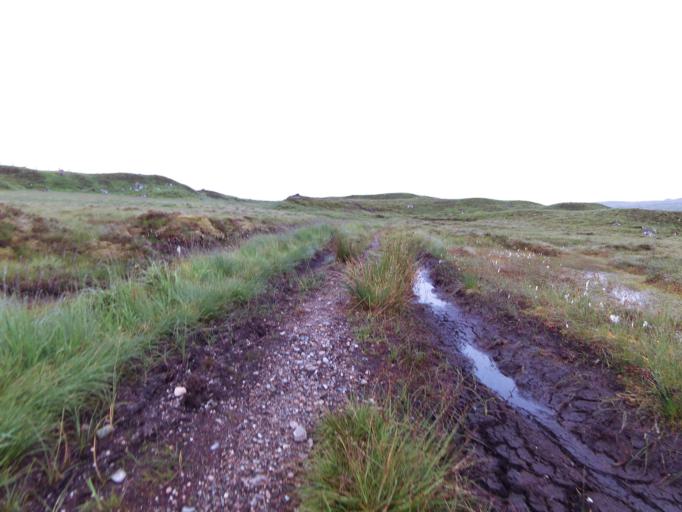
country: GB
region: Scotland
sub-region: Highland
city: Spean Bridge
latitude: 56.7650
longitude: -4.7006
